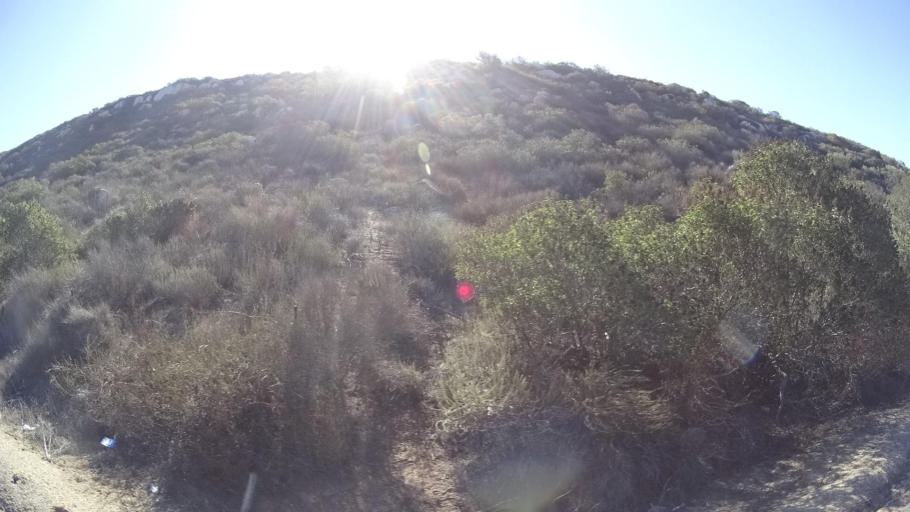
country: US
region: California
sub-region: San Diego County
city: Jamul
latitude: 32.6700
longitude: -116.7829
